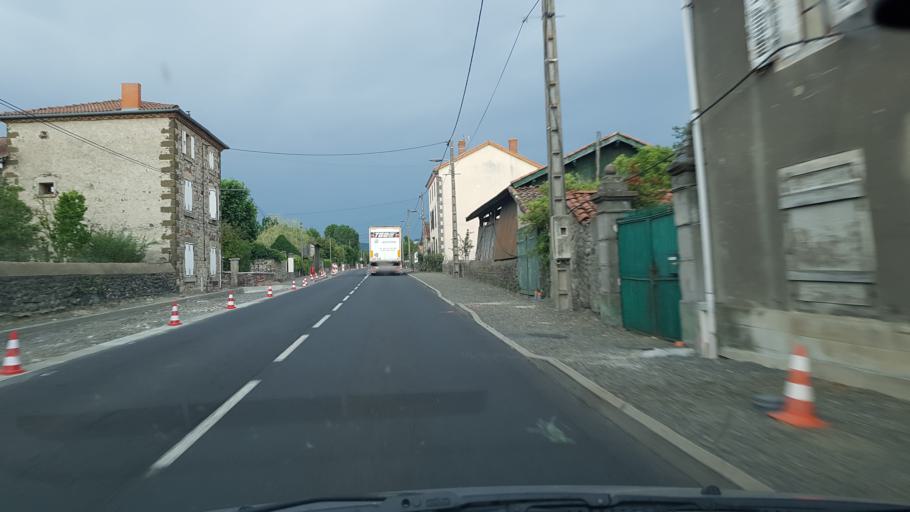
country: FR
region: Auvergne
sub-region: Departement de la Haute-Loire
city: Paulhaguet
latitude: 45.1550
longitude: 3.5421
